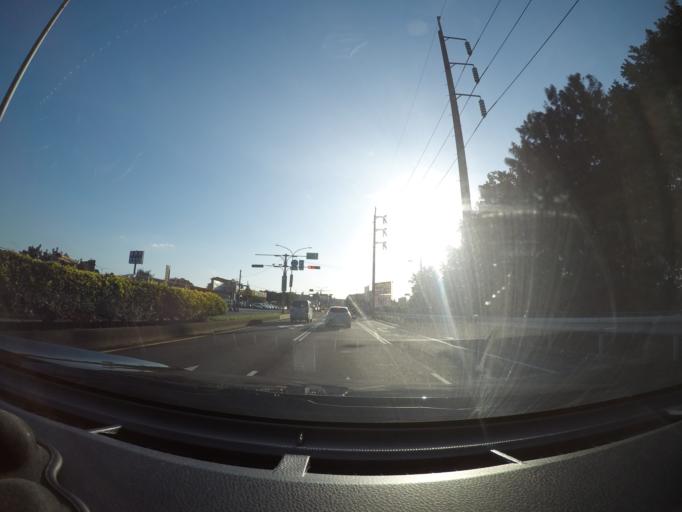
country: TW
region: Taiwan
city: Taoyuan City
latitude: 25.0714
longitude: 121.1976
